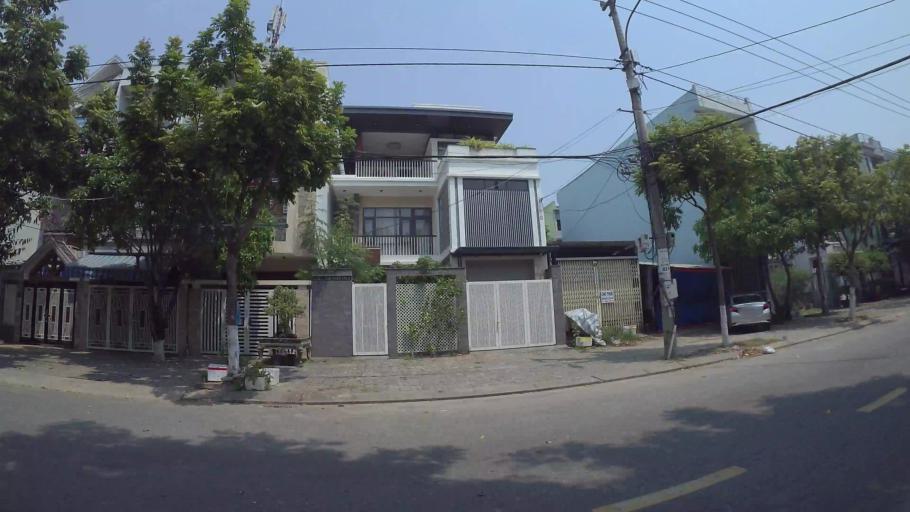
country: VN
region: Da Nang
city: Cam Le
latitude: 16.0213
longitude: 108.2148
